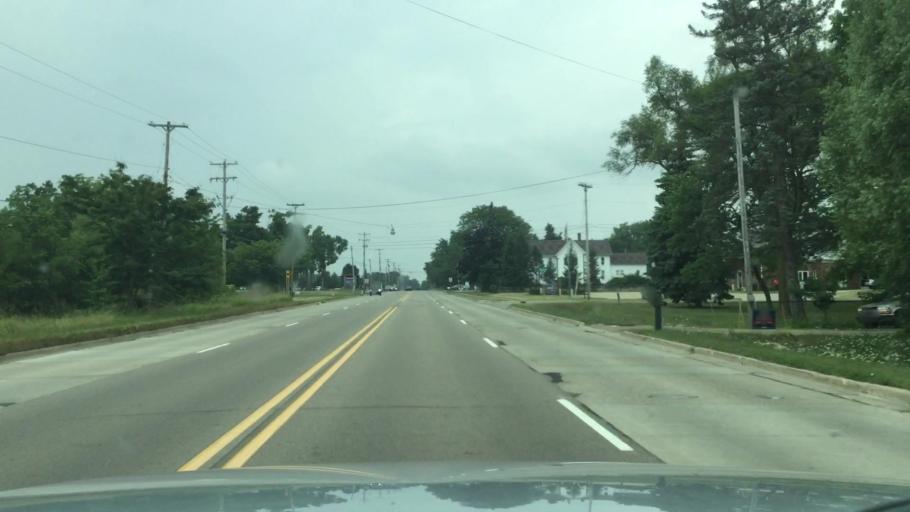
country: US
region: Michigan
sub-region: Shiawassee County
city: Owosso
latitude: 43.0219
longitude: -84.1769
